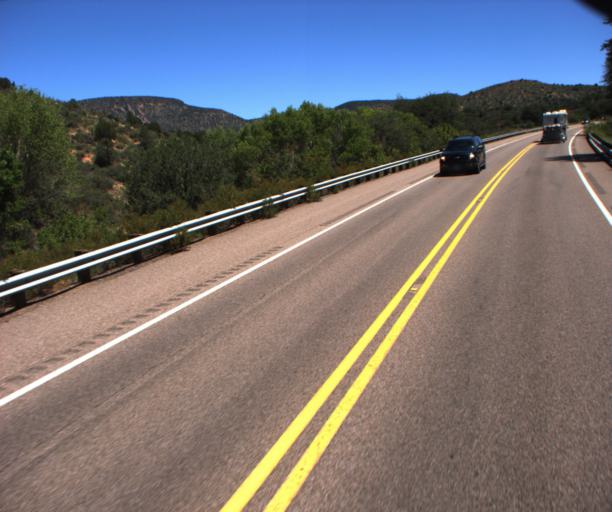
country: US
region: Arizona
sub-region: Gila County
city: Globe
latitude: 33.6224
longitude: -110.5994
